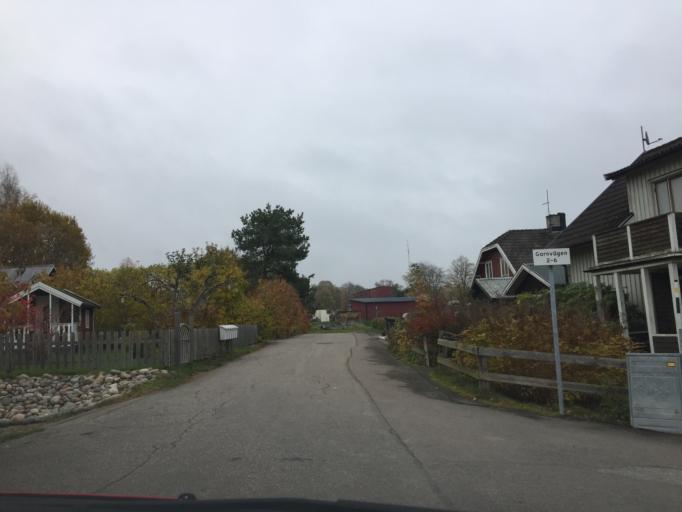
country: SE
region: Vaestra Goetaland
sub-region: Trollhattan
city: Sjuntorp
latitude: 58.1977
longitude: 12.2179
